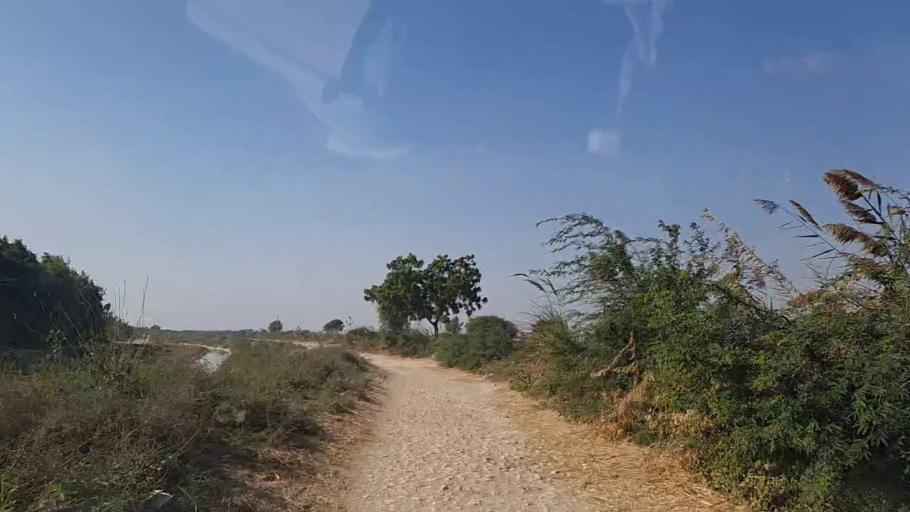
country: PK
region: Sindh
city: Thatta
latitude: 24.7675
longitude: 67.9350
